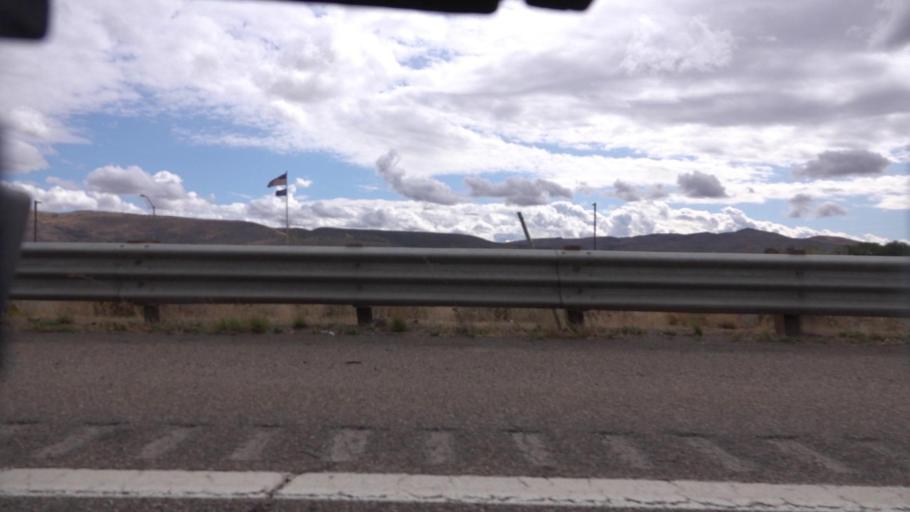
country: US
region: Nevada
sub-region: Elko County
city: Elko
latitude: 40.8639
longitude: -115.7346
